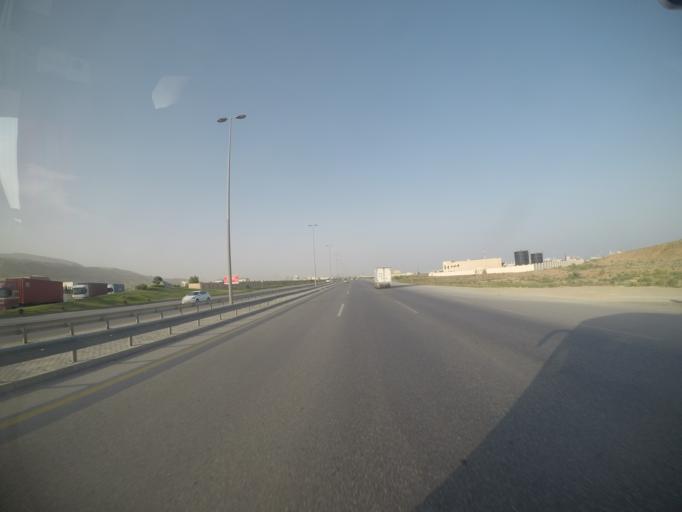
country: AZ
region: Baki
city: Korgoz
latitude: 40.2559
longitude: 49.6305
